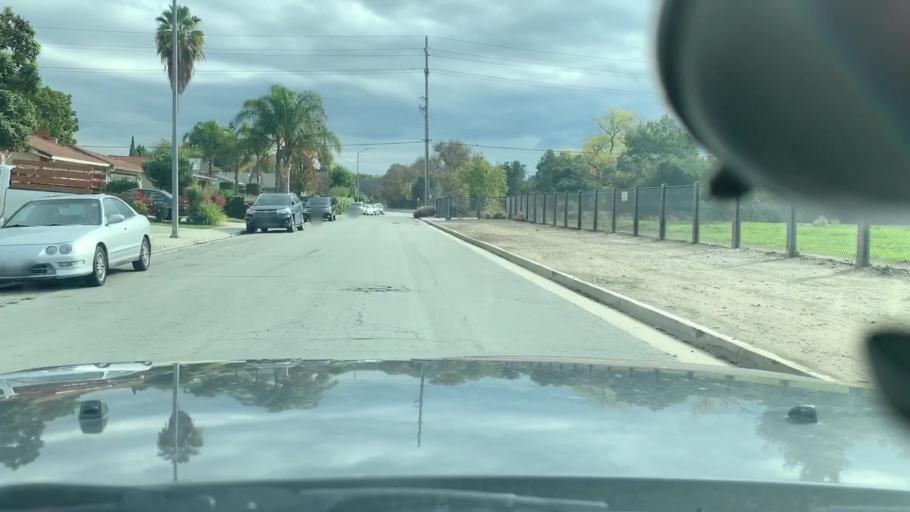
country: US
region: California
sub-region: Santa Clara County
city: Seven Trees
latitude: 37.3228
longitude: -121.8535
